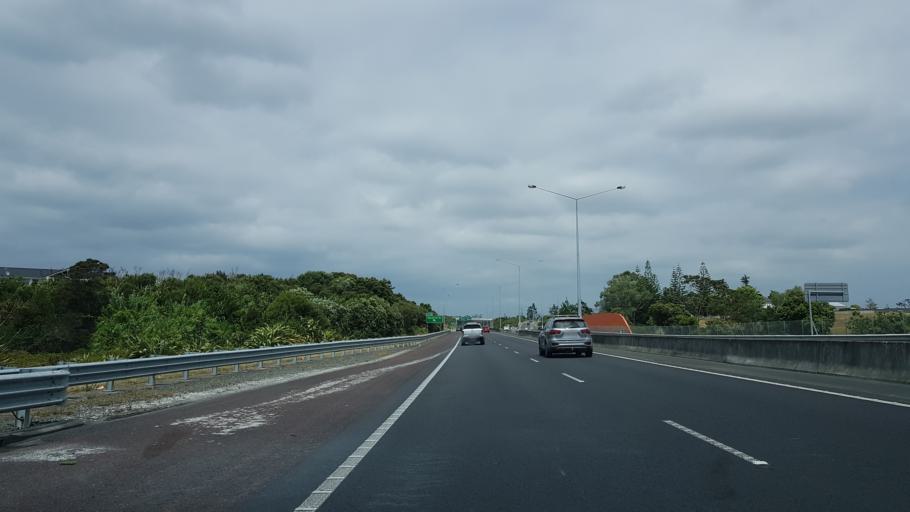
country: NZ
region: Auckland
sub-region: Auckland
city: Rosebank
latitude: -36.7874
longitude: 174.6607
